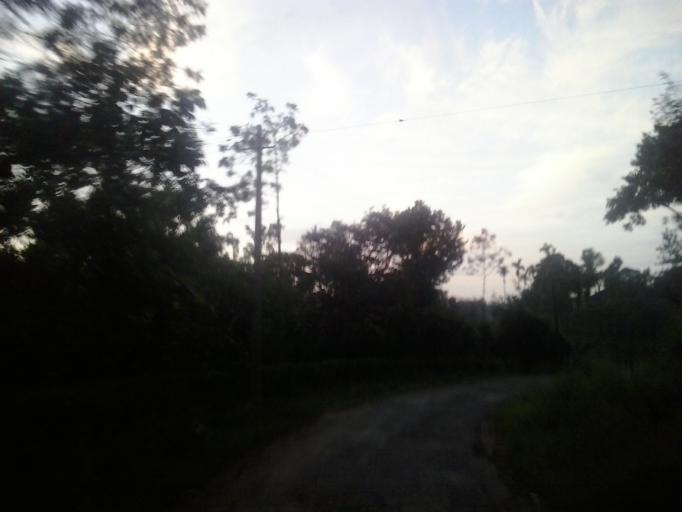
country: IN
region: Karnataka
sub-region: Chikmagalur
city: Mudigere
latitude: 13.0112
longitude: 75.6696
